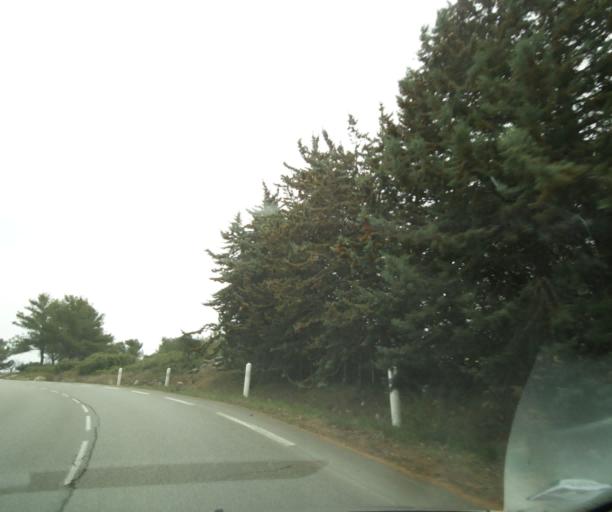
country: FR
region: Provence-Alpes-Cote d'Azur
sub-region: Departement des Bouches-du-Rhone
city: Belcodene
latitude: 43.4190
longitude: 5.6126
